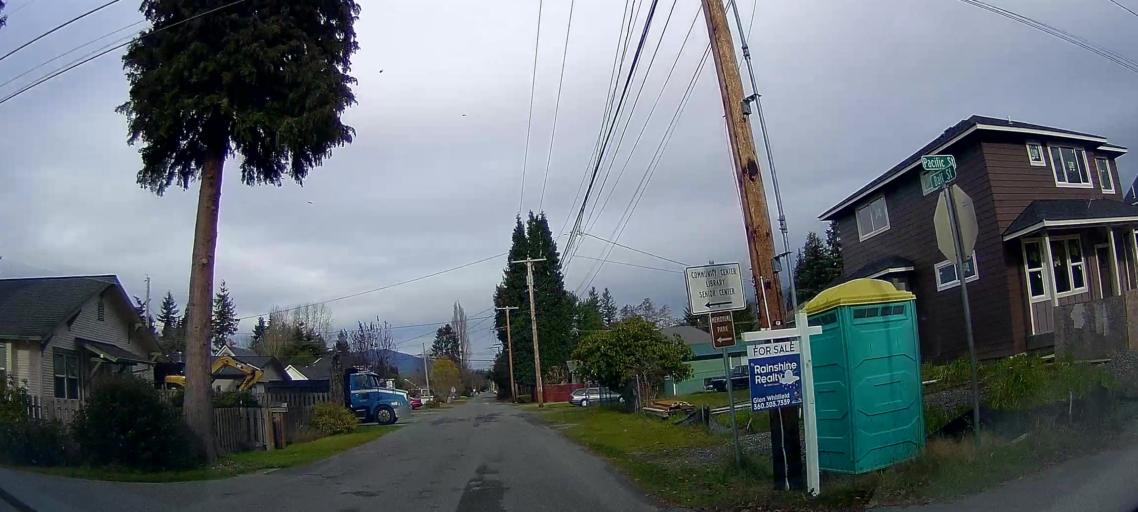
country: US
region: Washington
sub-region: Skagit County
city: Sedro-Woolley
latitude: 48.5043
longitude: -122.2287
